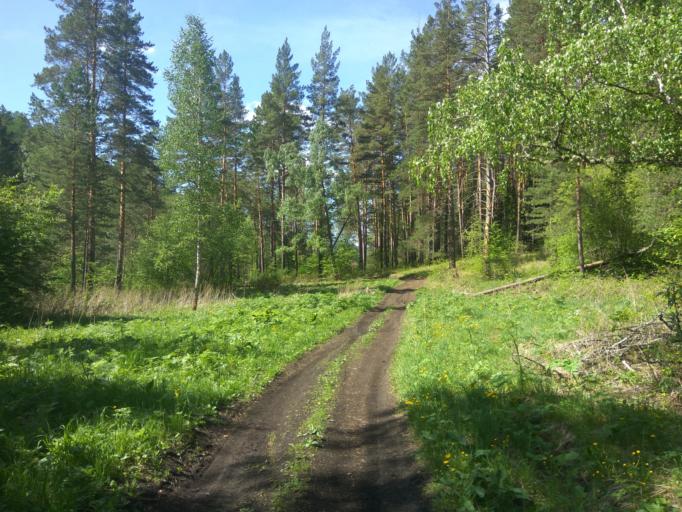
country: RU
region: Krasnoyarskiy
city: Krasnoyarsk
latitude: 55.9085
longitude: 92.9540
